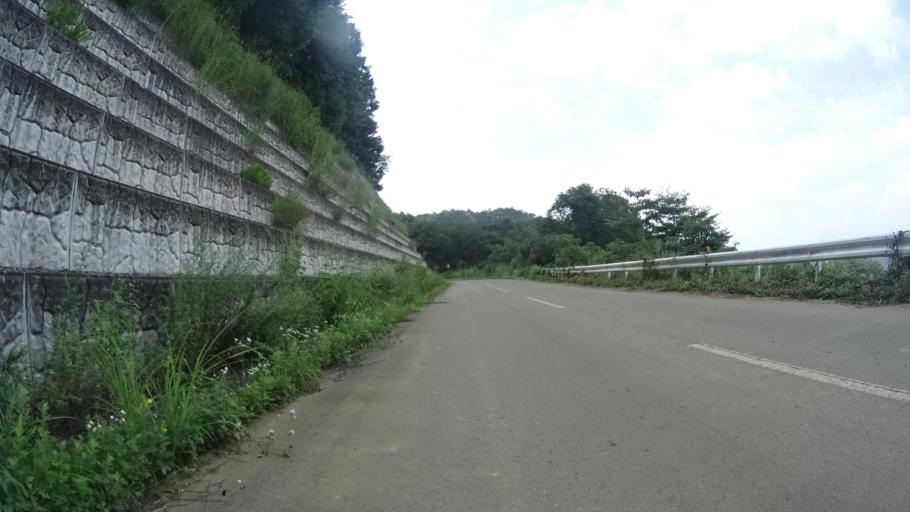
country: JP
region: Yamanashi
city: Nirasaki
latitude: 35.9073
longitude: 138.4637
